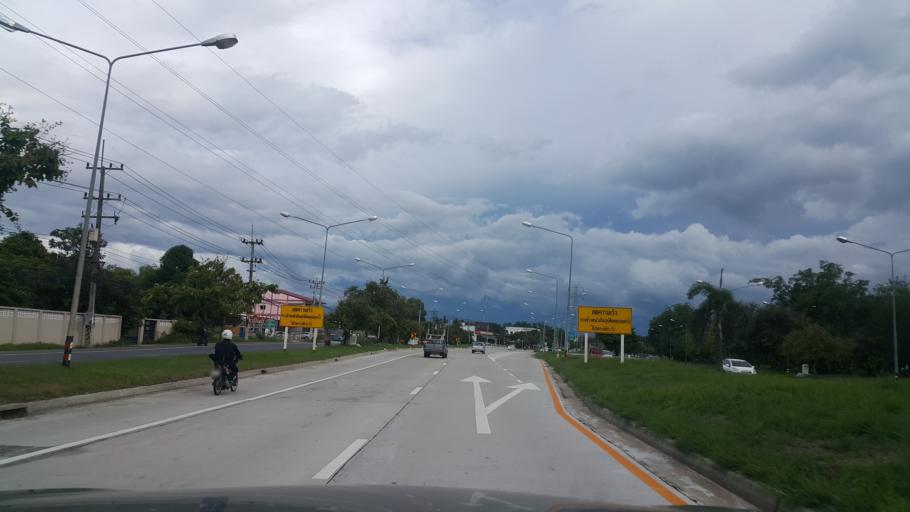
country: TH
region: Tak
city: Tak
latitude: 16.8950
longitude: 99.1288
